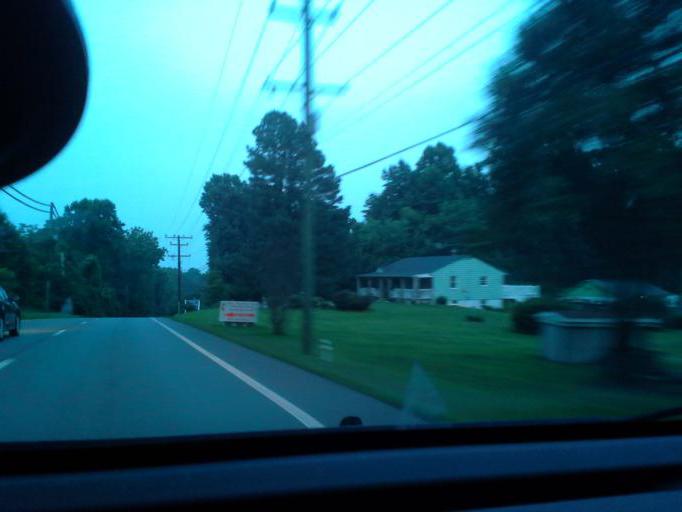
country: US
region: Maryland
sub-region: Calvert County
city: Owings
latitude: 38.7036
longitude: -76.5711
